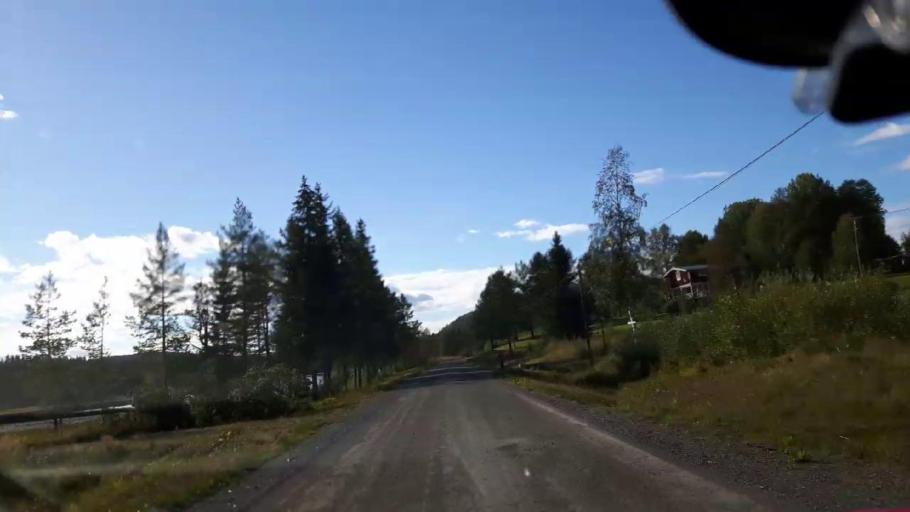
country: SE
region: Jaemtland
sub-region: Ragunda Kommun
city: Hammarstrand
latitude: 63.4859
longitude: 16.1022
